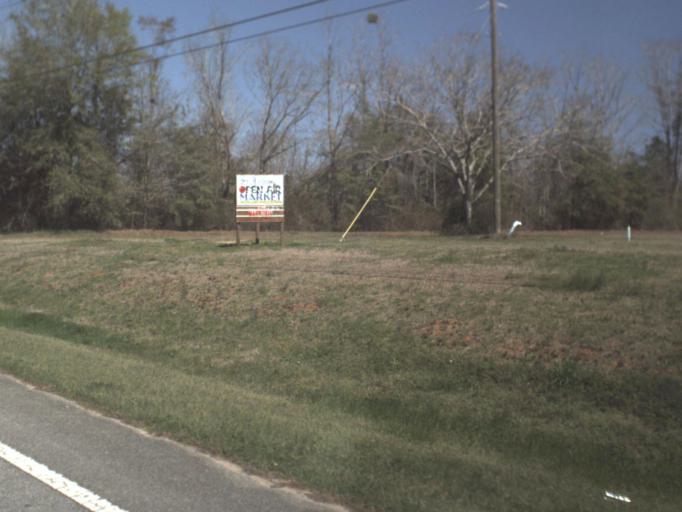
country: US
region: Florida
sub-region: Gadsden County
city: Quincy
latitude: 30.6461
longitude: -84.6006
